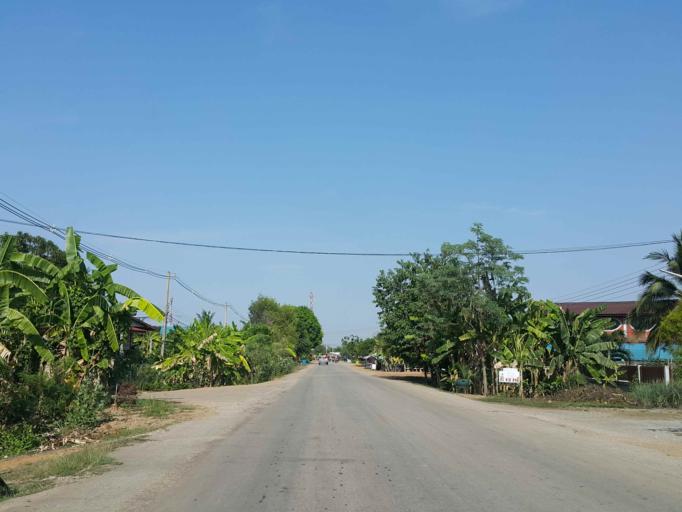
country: TH
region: Sukhothai
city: Thung Saliam
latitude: 17.3267
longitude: 99.6245
